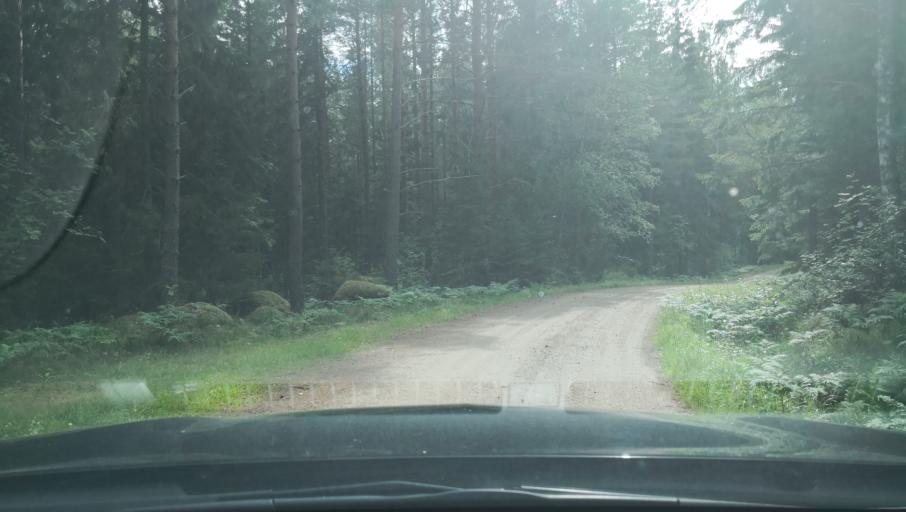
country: SE
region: Vaestmanland
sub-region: Hallstahammars Kommun
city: Hallstahammar
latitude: 59.6414
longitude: 16.0821
